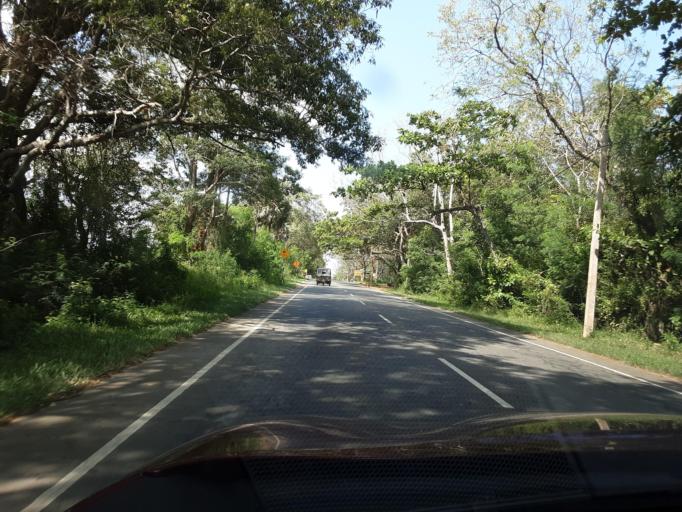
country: LK
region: Southern
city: Tangalla
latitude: 6.2266
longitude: 81.2216
